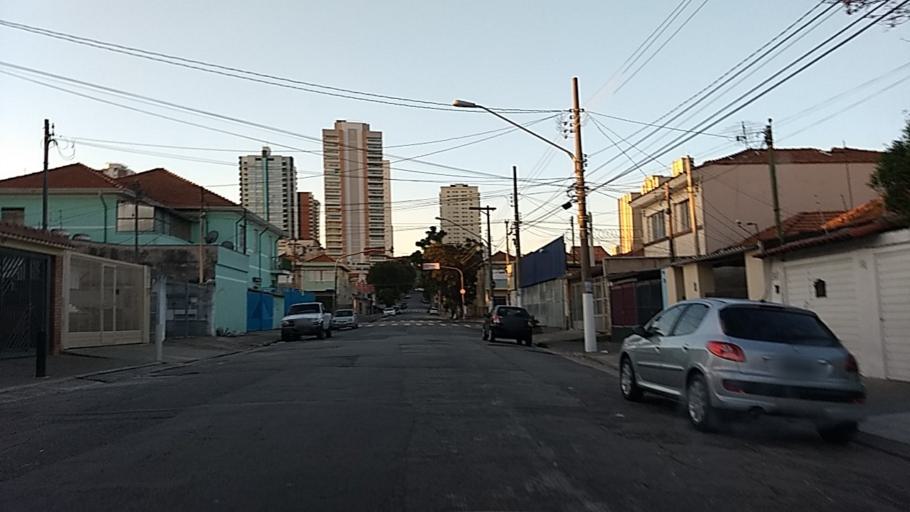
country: BR
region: Sao Paulo
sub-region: Sao Paulo
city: Sao Paulo
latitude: -23.5080
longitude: -46.6032
